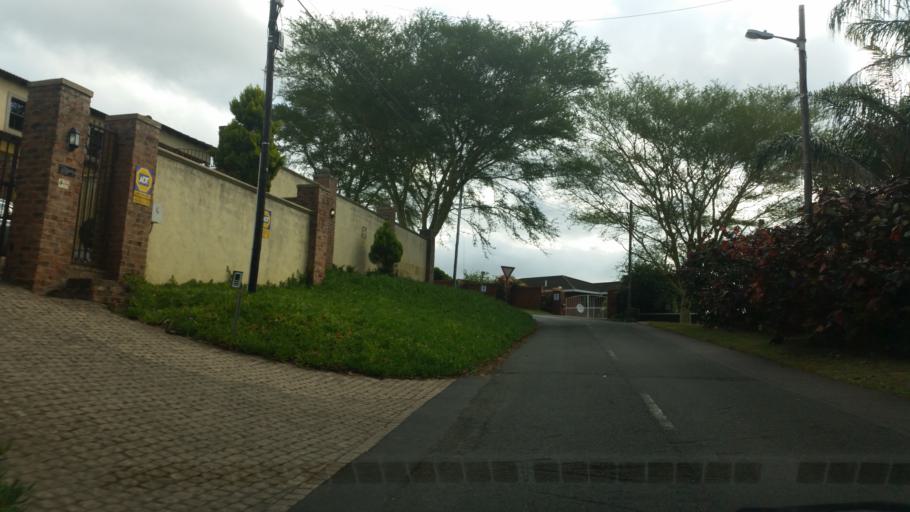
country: ZA
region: KwaZulu-Natal
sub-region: eThekwini Metropolitan Municipality
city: Berea
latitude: -29.8271
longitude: 30.9362
